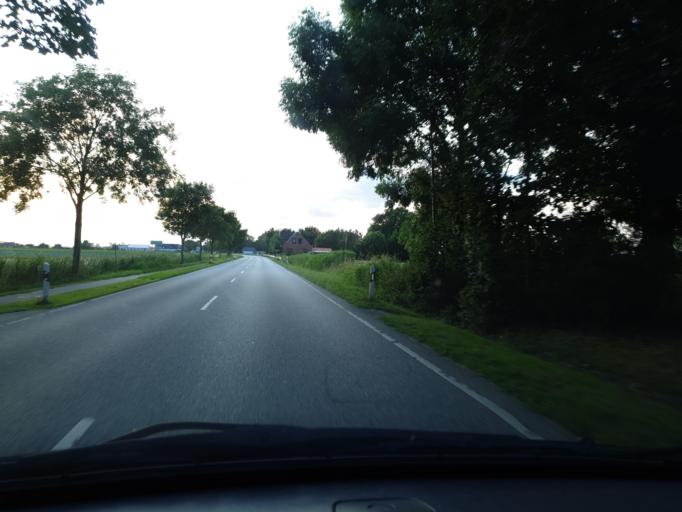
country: DE
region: Schleswig-Holstein
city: Schmedeswurth
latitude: 53.9215
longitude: 9.0457
